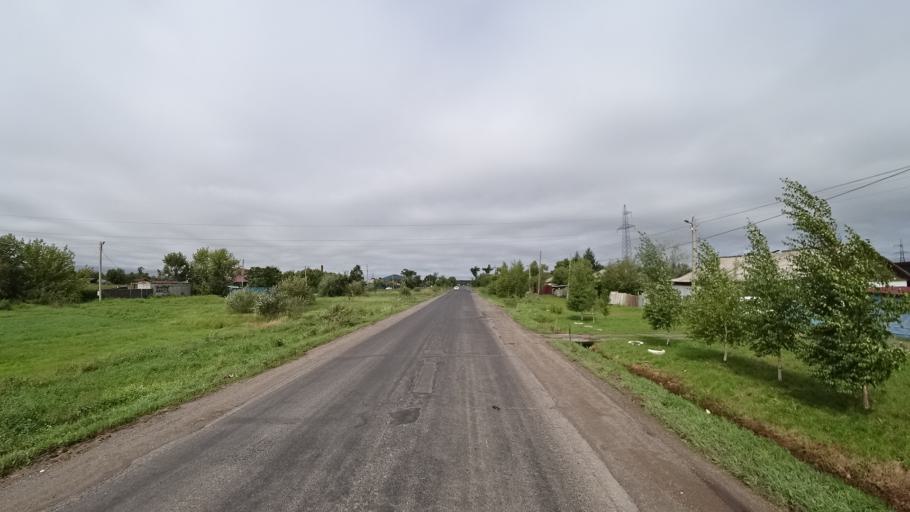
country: RU
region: Primorskiy
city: Monastyrishche
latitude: 44.1997
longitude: 132.4770
